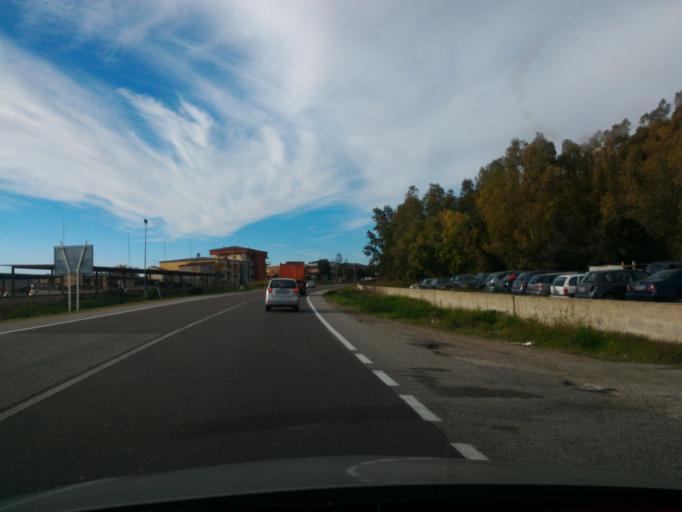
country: IT
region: Calabria
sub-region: Provincia di Crotone
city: Crotone
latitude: 39.0603
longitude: 17.0988
